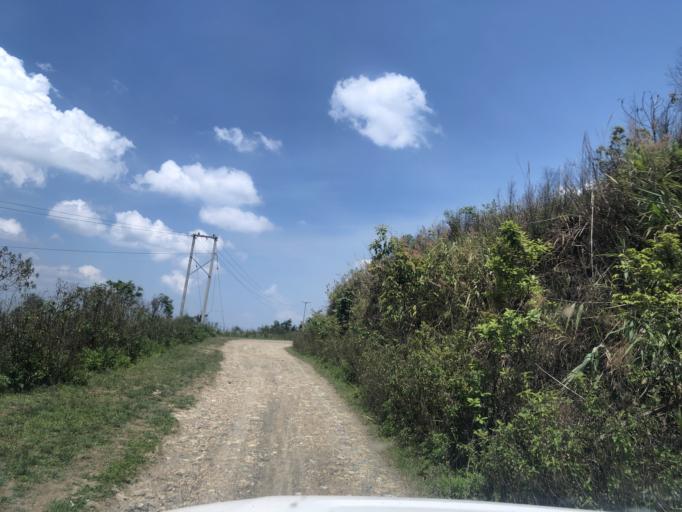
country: LA
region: Phongsali
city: Phongsali
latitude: 21.4214
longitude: 102.1811
